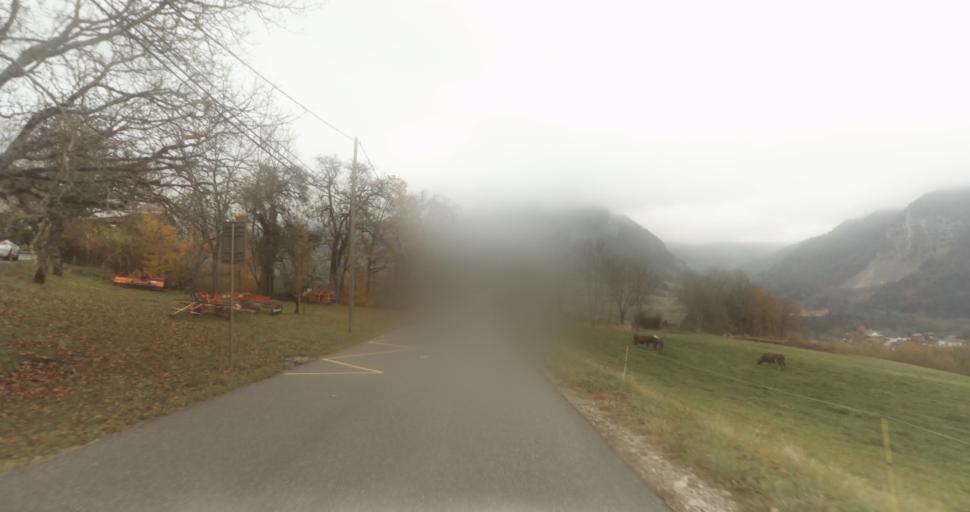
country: FR
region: Rhone-Alpes
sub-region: Departement de la Haute-Savoie
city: Thorens-Glieres
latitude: 46.0026
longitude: 6.2465
